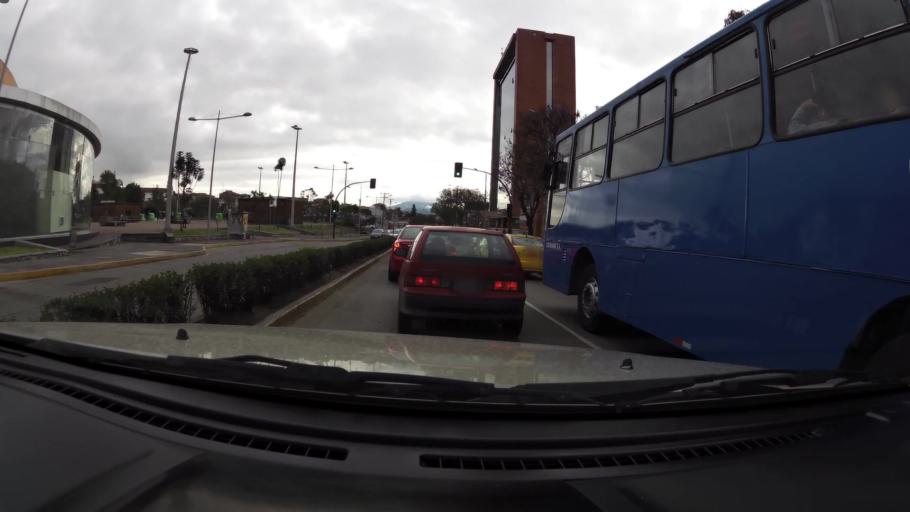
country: EC
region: Azuay
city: Cuenca
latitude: -2.9054
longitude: -79.0042
